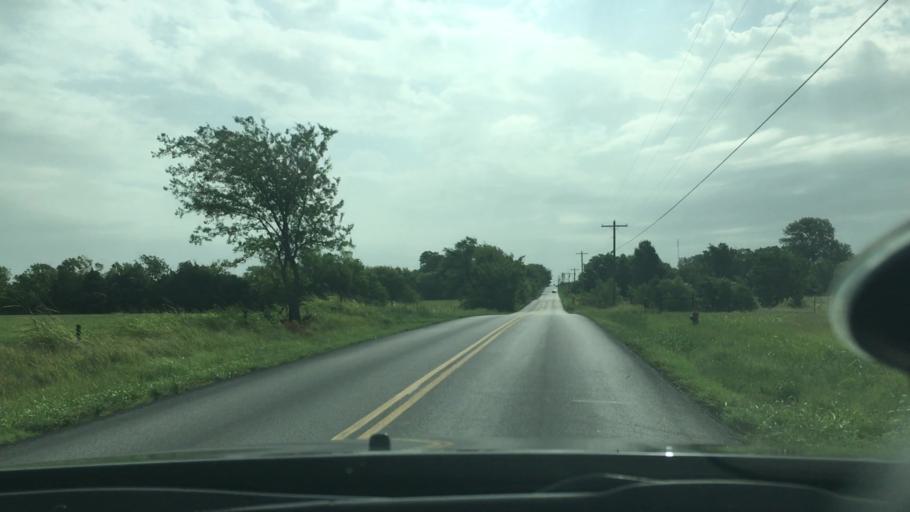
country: US
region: Oklahoma
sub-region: Carter County
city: Ardmore
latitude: 34.2020
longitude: -97.1894
